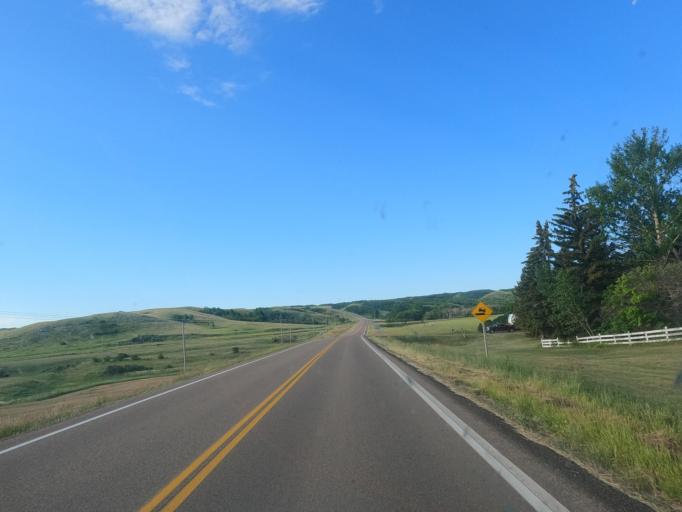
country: CA
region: Saskatchewan
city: Assiniboia
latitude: 49.3876
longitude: -105.6377
